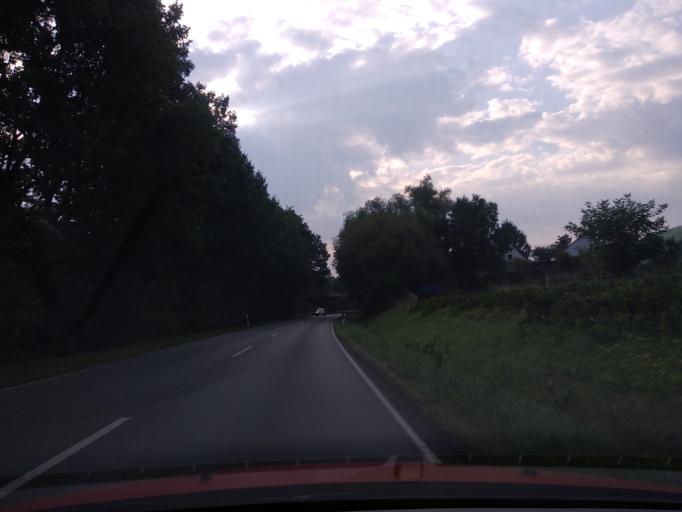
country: DE
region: Hesse
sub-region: Regierungsbezirk Kassel
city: Calden
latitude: 51.3705
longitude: 9.3948
